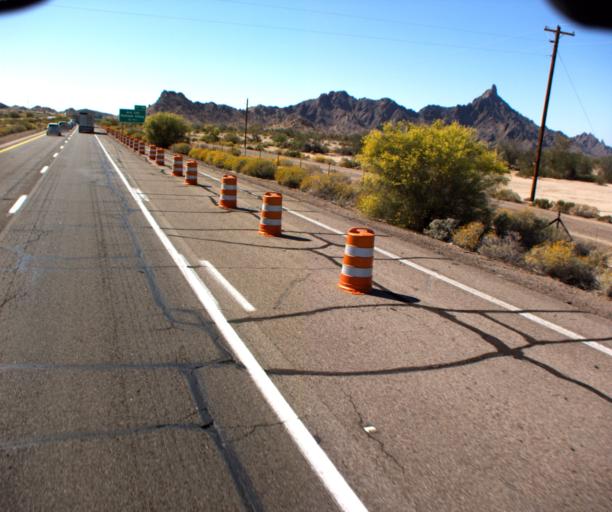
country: US
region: Arizona
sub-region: Yuma County
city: Wellton
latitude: 32.7305
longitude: -113.7204
